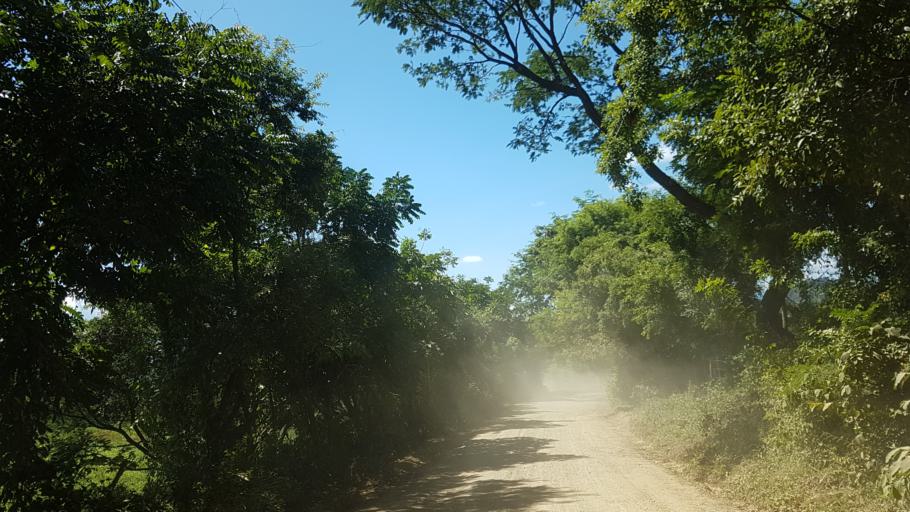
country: HN
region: El Paraiso
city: Santa Cruz
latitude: 13.7339
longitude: -86.6771
